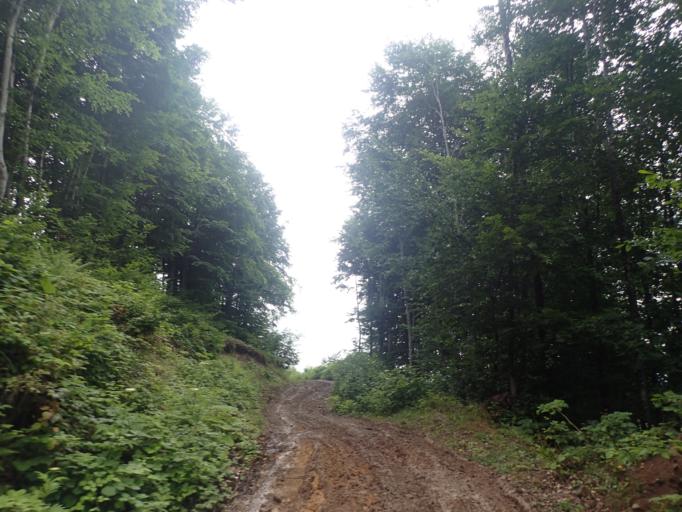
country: TR
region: Ordu
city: Akkus
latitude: 40.8047
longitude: 37.0896
